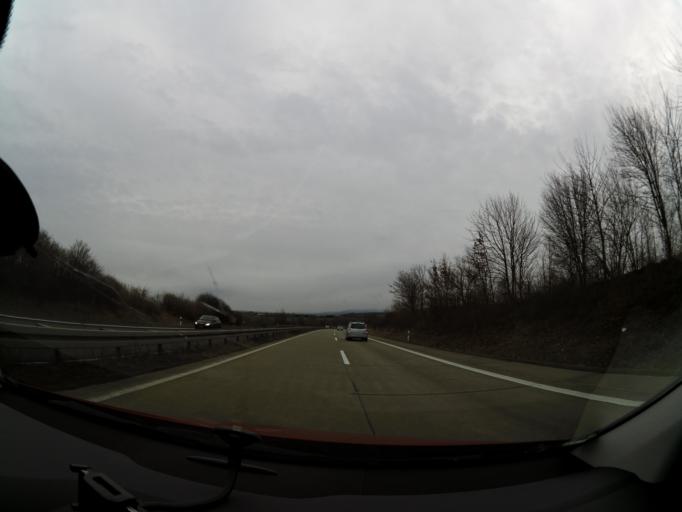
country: DE
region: Lower Saxony
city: Schladen
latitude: 51.9976
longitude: 10.5512
